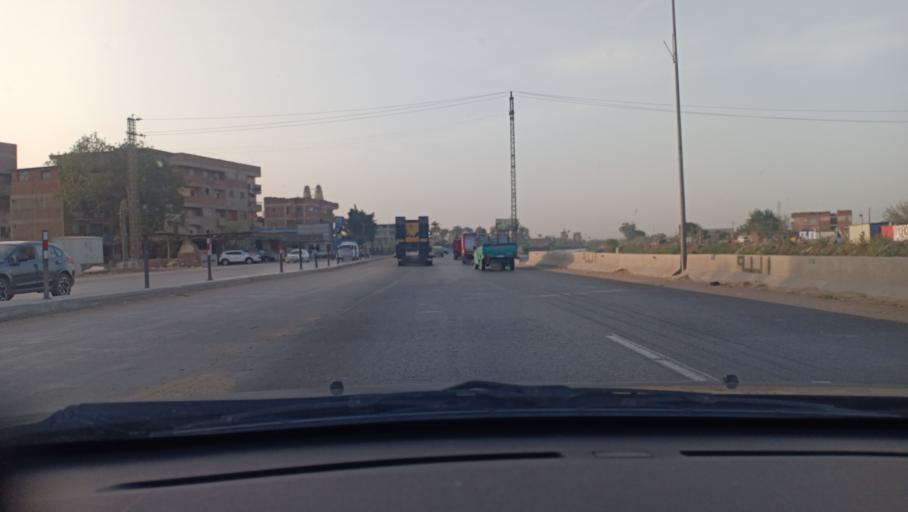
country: EG
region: Muhafazat al Minufiyah
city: Quwaysina
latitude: 30.5518
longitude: 31.2687
